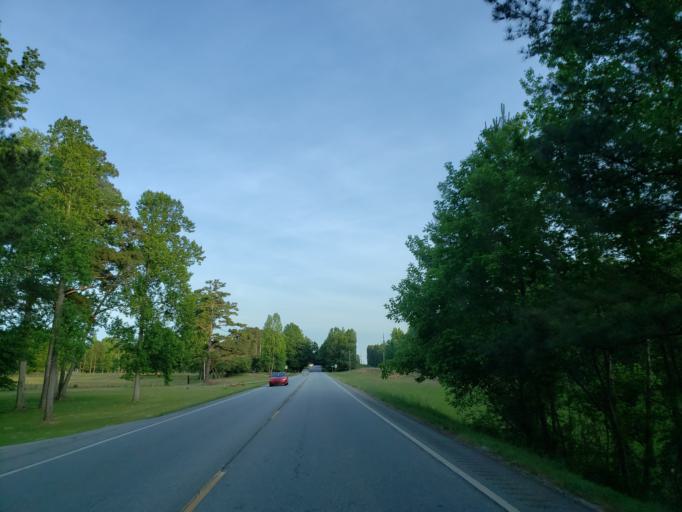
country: US
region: Georgia
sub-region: Coweta County
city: Newnan
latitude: 33.4429
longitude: -84.8779
